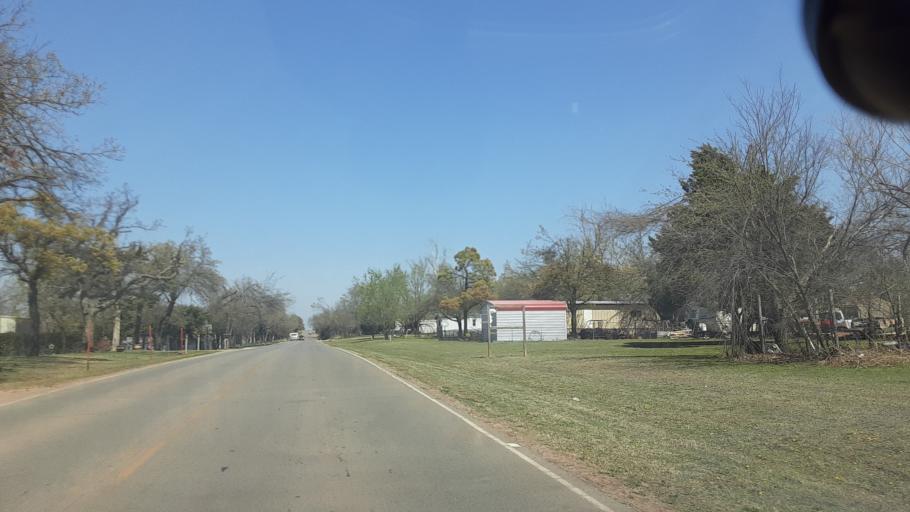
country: US
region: Oklahoma
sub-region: Oklahoma County
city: Edmond
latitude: 35.7588
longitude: -97.4784
